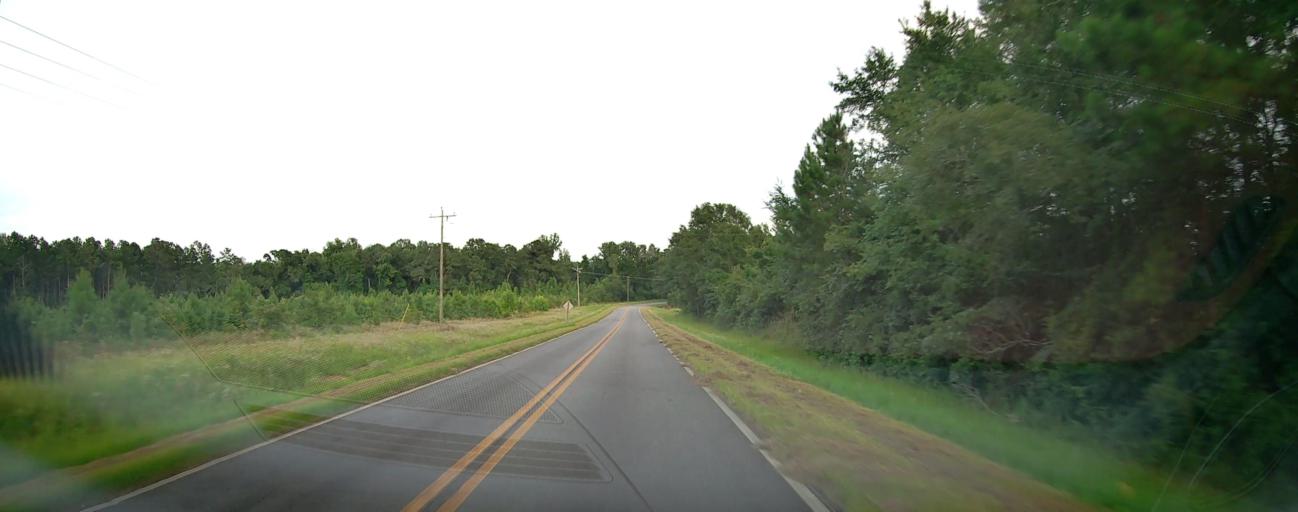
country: US
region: Georgia
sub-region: Crawford County
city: Roberta
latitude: 32.6702
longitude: -84.0717
